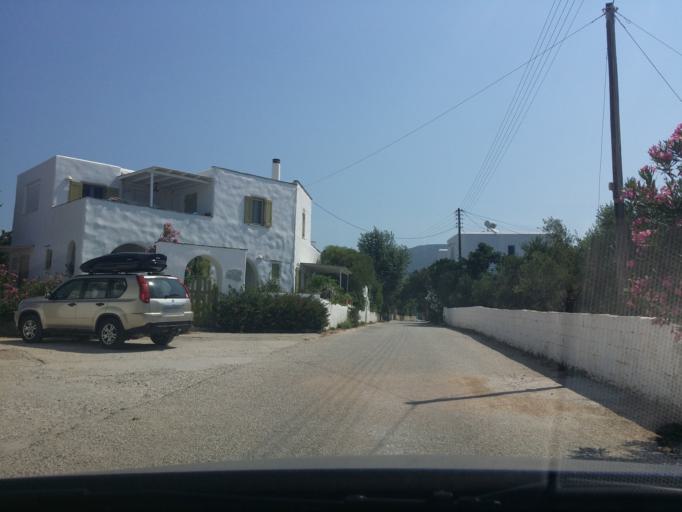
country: GR
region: South Aegean
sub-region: Nomos Kykladon
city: Antiparos
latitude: 36.9975
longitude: 25.1394
